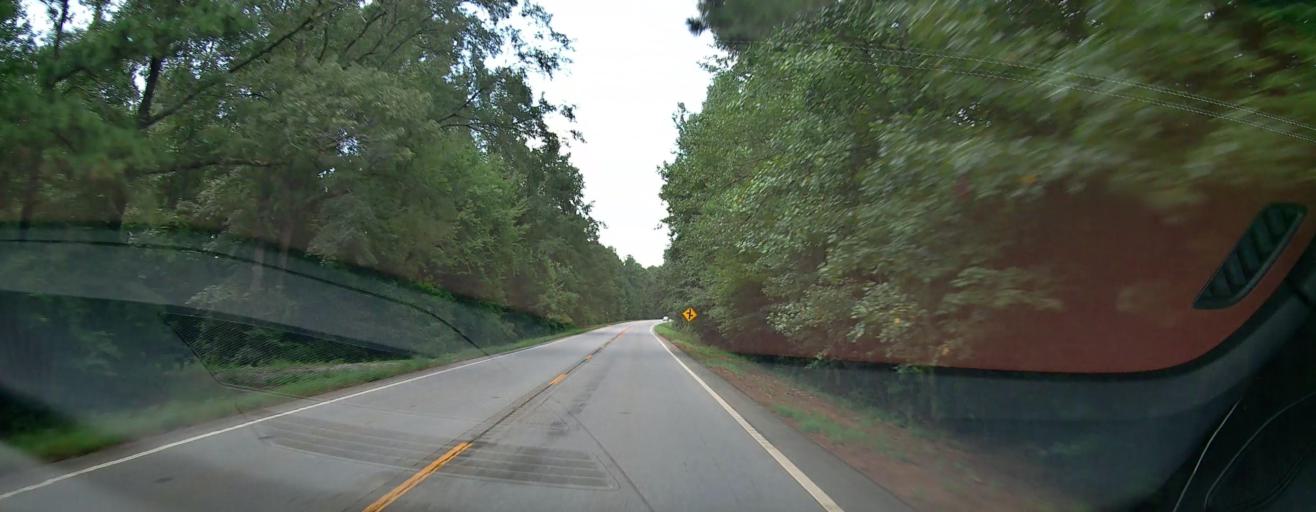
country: US
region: Georgia
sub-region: Coweta County
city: Senoia
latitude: 33.2412
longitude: -84.5661
